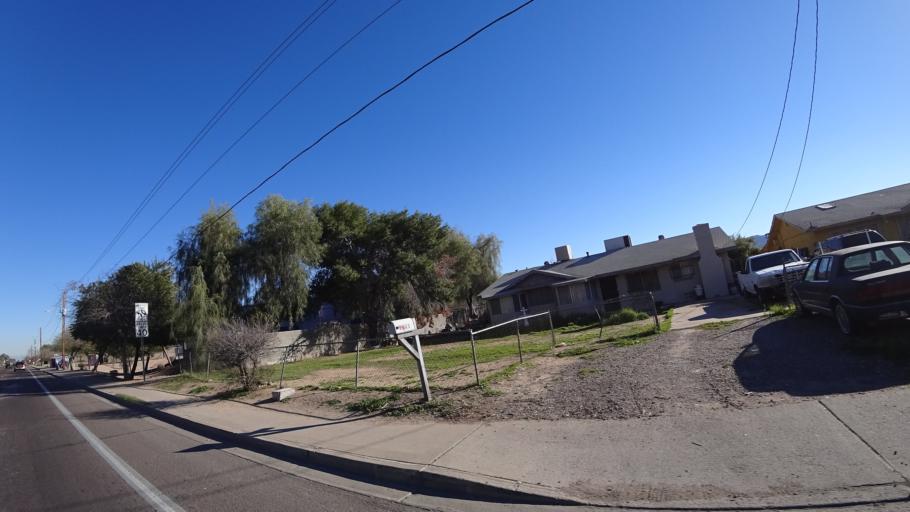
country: US
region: Arizona
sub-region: Maricopa County
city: Phoenix
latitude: 33.3928
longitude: -112.0379
